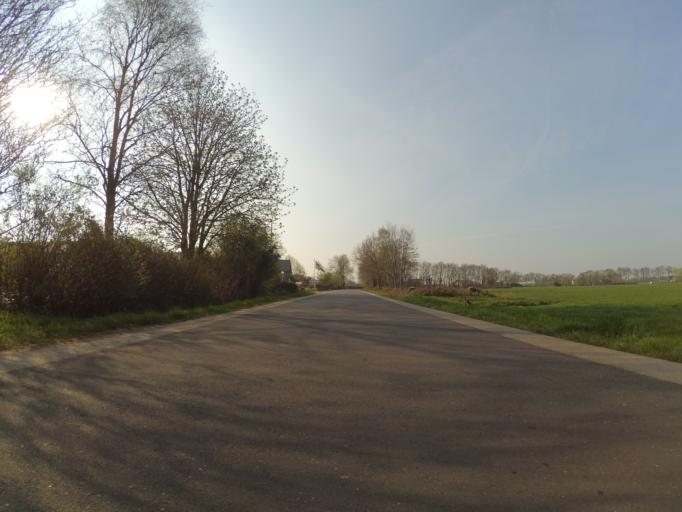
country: NL
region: Gelderland
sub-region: Gemeente Barneveld
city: Voorthuizen
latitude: 52.1899
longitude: 5.5810
